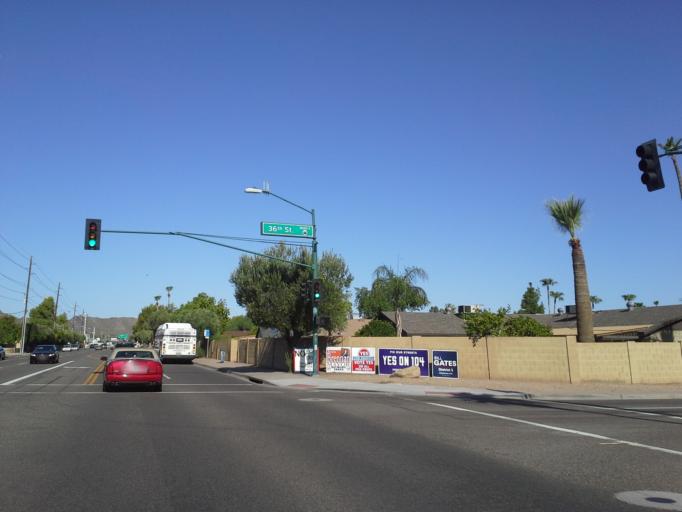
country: US
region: Arizona
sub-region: Maricopa County
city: Paradise Valley
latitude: 33.5826
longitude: -112.0041
